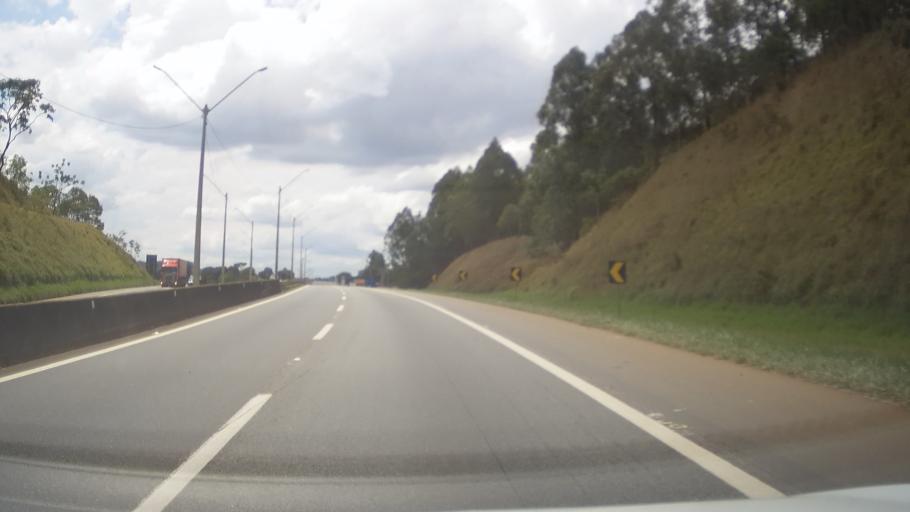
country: BR
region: Minas Gerais
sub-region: Nepomuceno
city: Nepomuceno
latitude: -21.2701
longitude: -45.1361
